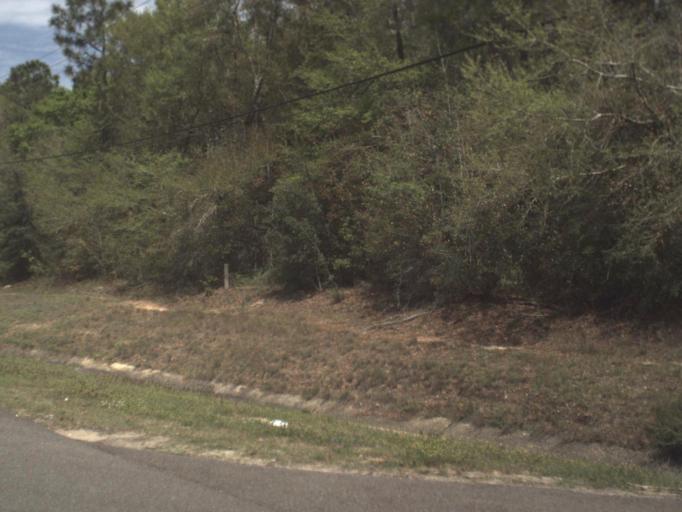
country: US
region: Florida
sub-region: Okaloosa County
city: Crestview
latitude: 30.7593
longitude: -86.5455
